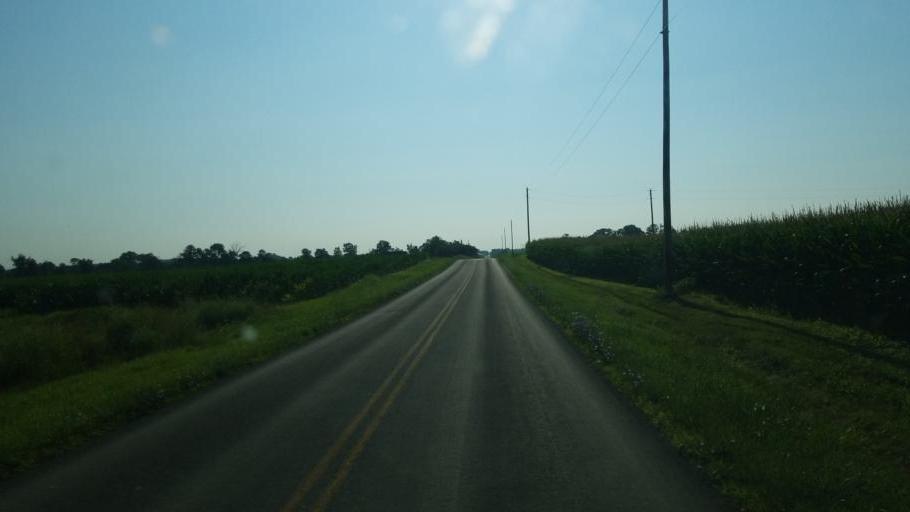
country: US
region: Ohio
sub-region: Hardin County
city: Kenton
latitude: 40.5614
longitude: -83.5623
